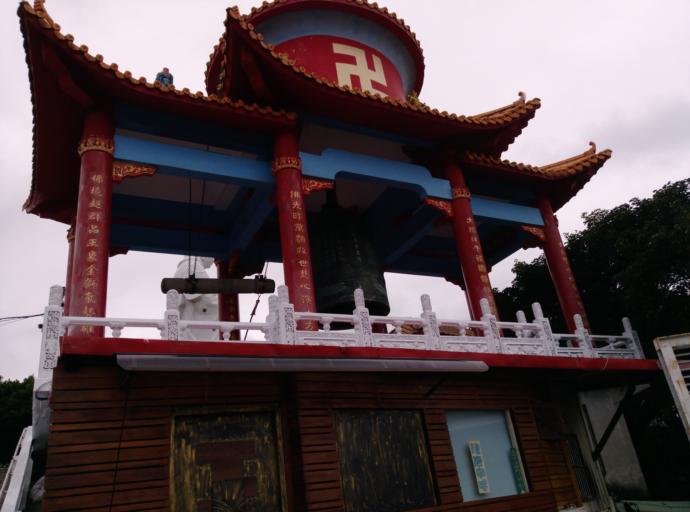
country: TW
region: Taiwan
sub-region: Keelung
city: Keelung
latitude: 25.1336
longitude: 121.7512
